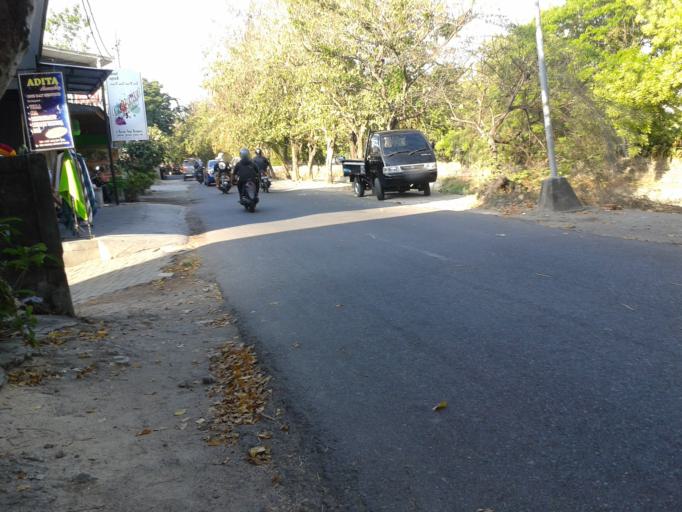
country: ID
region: Bali
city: Kuta
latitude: -8.6999
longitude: 115.1717
